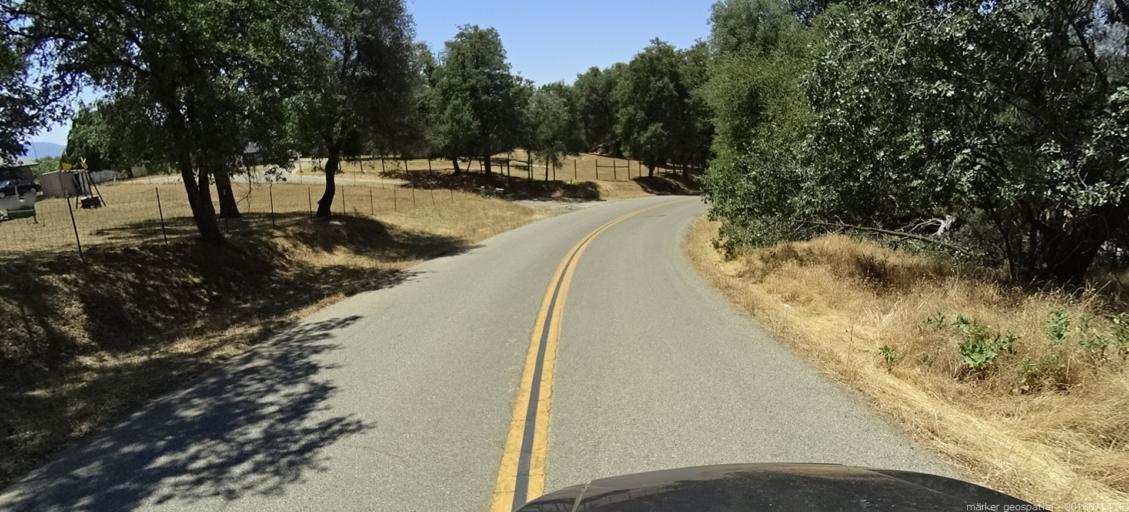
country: US
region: California
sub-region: Madera County
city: Ahwahnee
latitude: 37.4015
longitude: -119.7028
